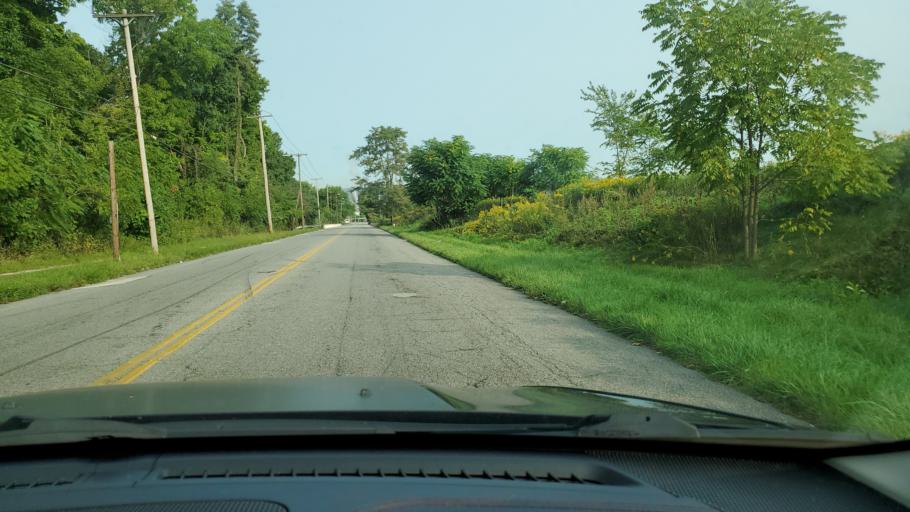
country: US
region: Ohio
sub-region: Mahoning County
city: Campbell
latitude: 41.0720
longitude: -80.6214
